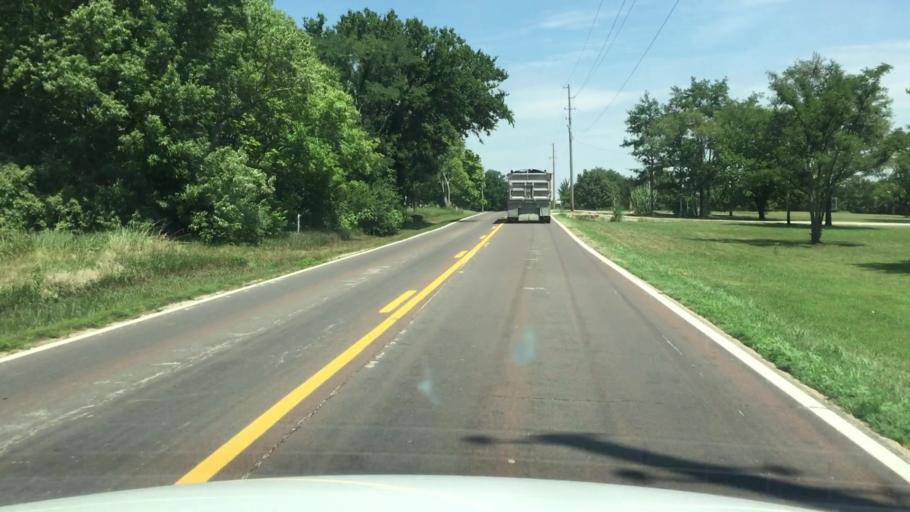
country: US
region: Kansas
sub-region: Shawnee County
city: Topeka
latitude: 38.9860
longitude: -95.5255
